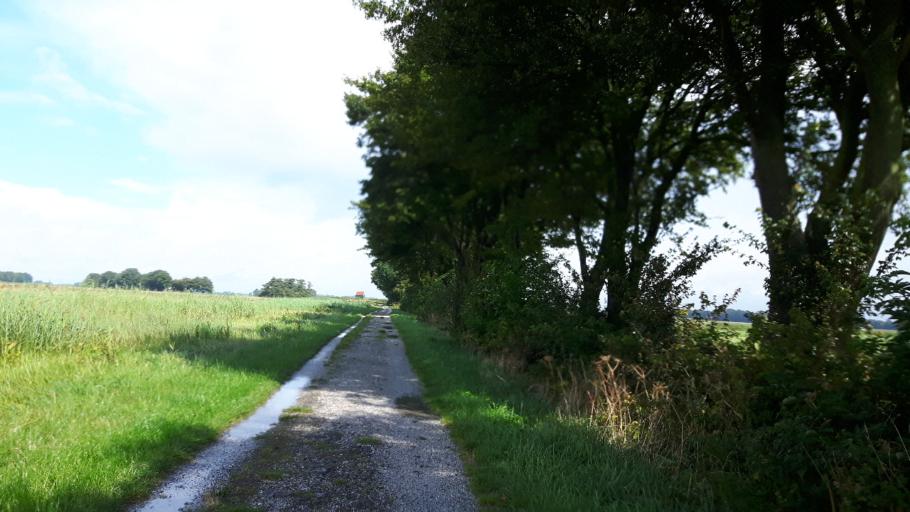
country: NL
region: Flevoland
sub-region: Gemeente Noordoostpolder
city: Ens
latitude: 52.6246
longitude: 5.7754
